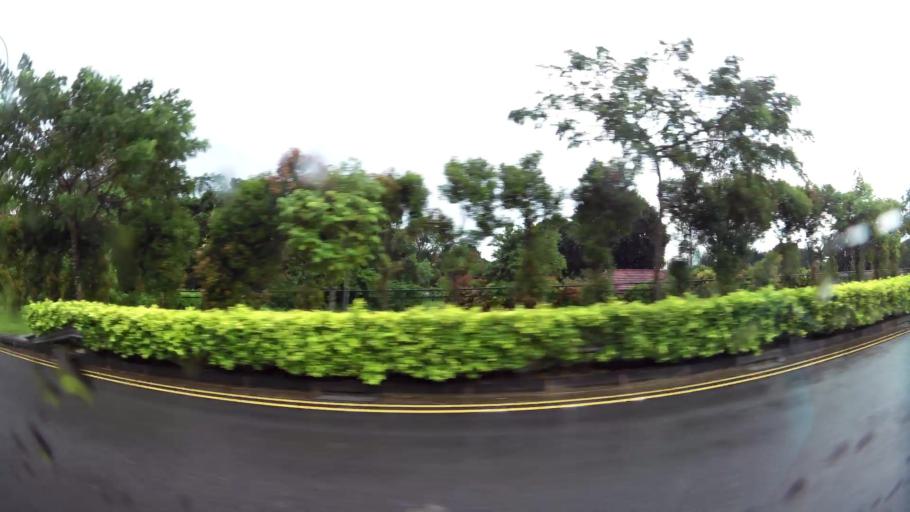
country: MY
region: Johor
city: Kampung Pasir Gudang Baru
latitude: 1.4027
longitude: 103.8690
